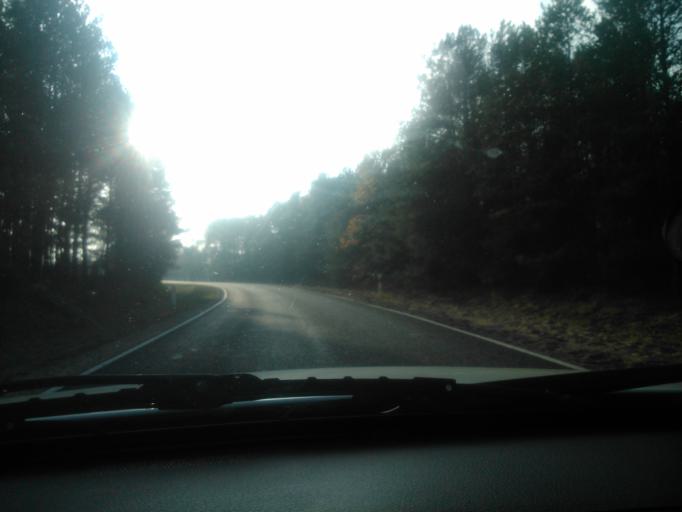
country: PL
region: Masovian Voivodeship
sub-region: Powiat ostrolecki
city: Czarnia
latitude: 53.3122
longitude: 21.1119
